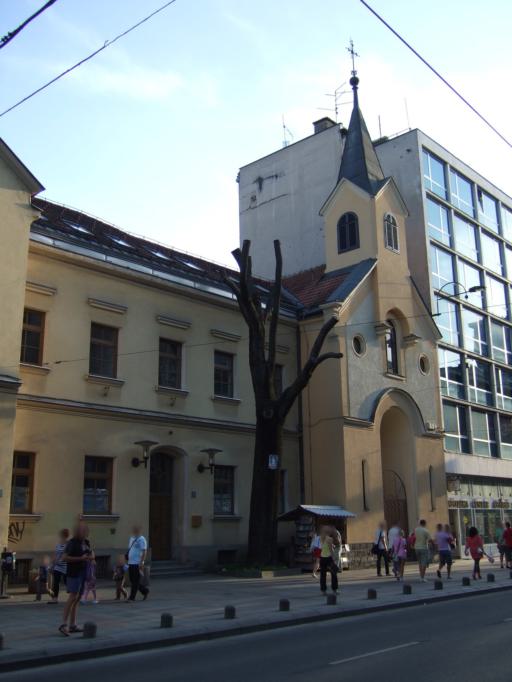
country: BA
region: Federation of Bosnia and Herzegovina
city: Kobilja Glava
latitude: 43.8588
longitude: 18.4194
